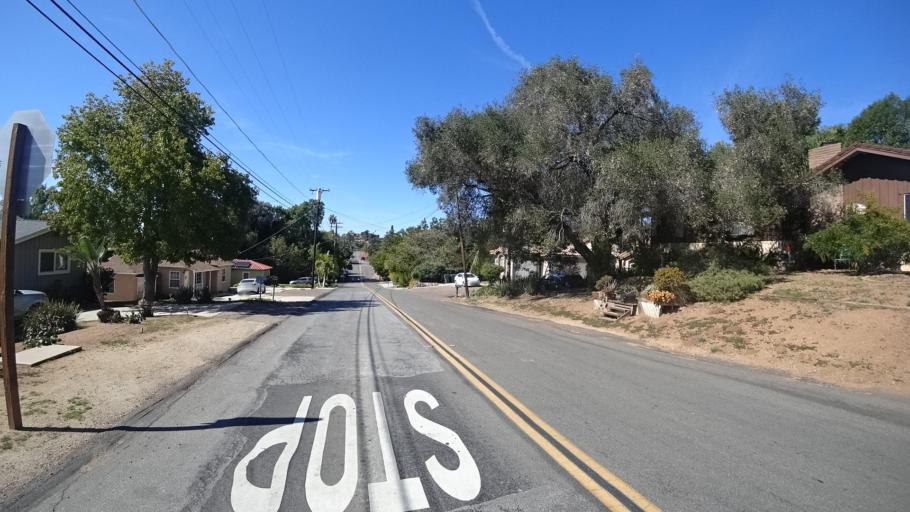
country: US
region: California
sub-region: San Diego County
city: Casa de Oro-Mount Helix
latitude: 32.7555
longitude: -116.9655
